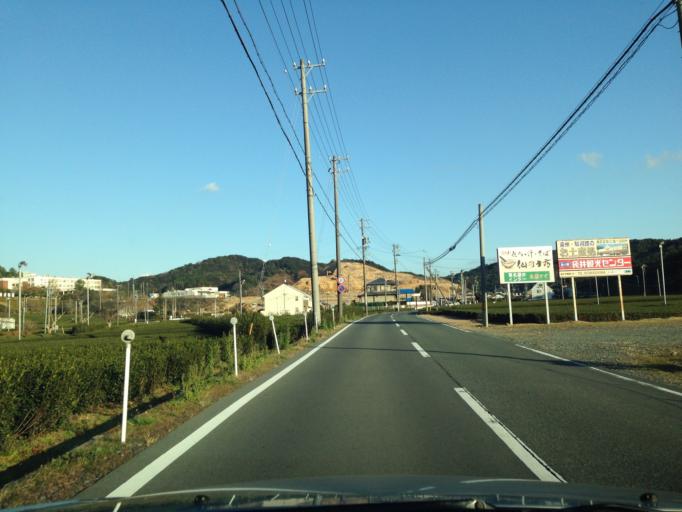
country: JP
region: Shizuoka
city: Fukuroi
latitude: 34.7363
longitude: 137.9556
